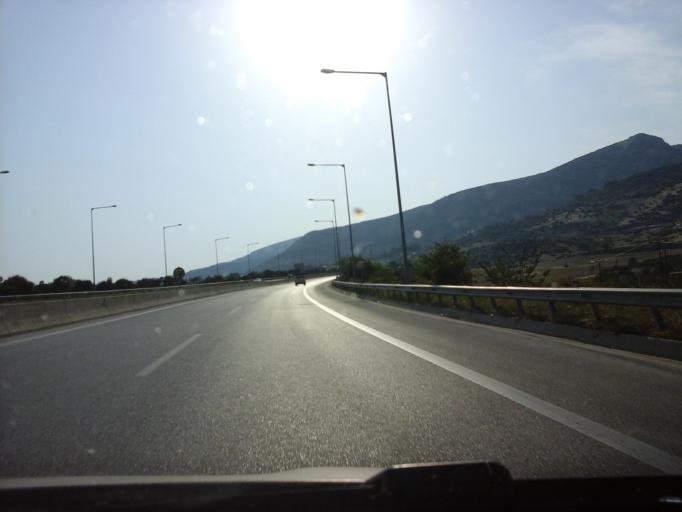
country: GR
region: East Macedonia and Thrace
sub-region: Nomos Kavalas
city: Chrysoupolis
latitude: 40.9892
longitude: 24.6303
